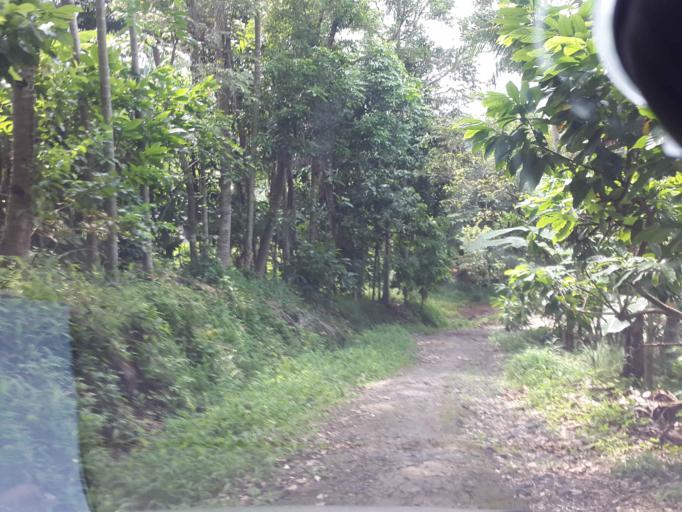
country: ID
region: Lampung
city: Penengahan
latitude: -5.8290
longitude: 105.6587
